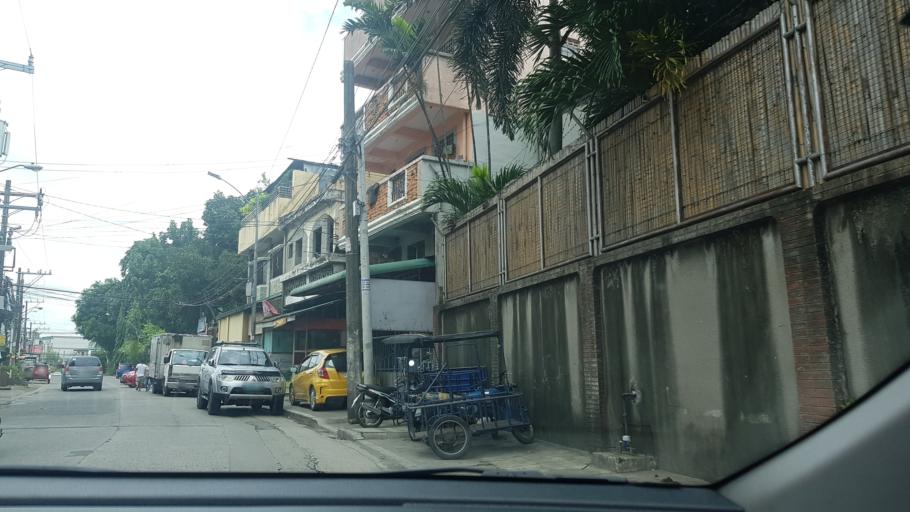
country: PH
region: Calabarzon
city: Del Monte
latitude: 14.6489
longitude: 121.0044
